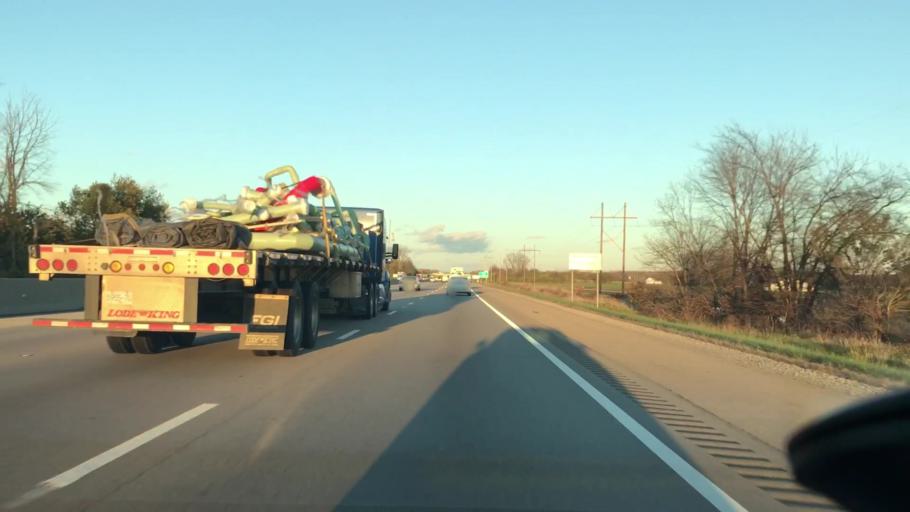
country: US
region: Ohio
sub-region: Clark County
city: Holiday Valley
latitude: 39.8730
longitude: -83.9778
